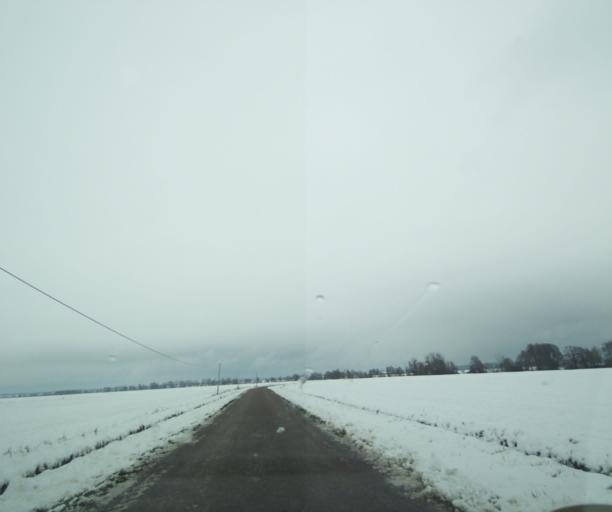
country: FR
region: Champagne-Ardenne
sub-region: Departement de la Haute-Marne
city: Montier-en-Der
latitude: 48.4295
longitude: 4.7895
